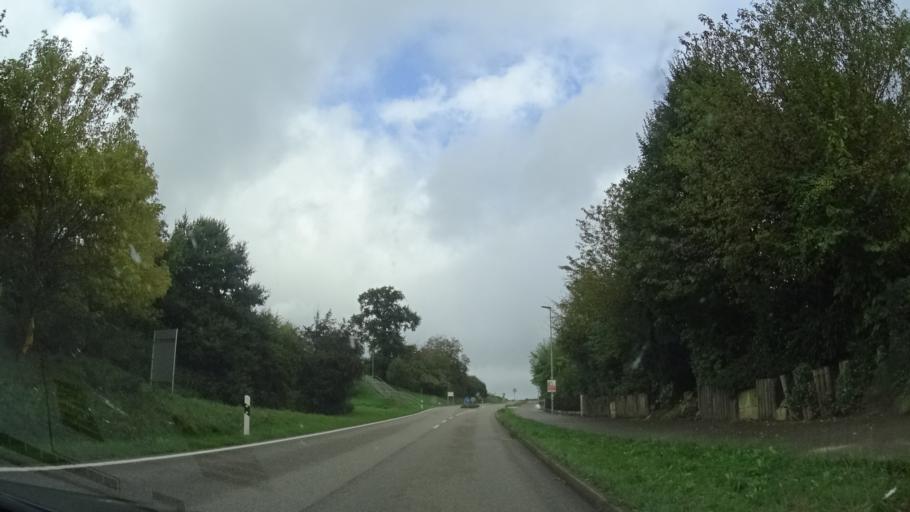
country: DE
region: Baden-Wuerttemberg
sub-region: Karlsruhe Region
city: Konigsbach-Stein
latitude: 48.9665
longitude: 8.6343
